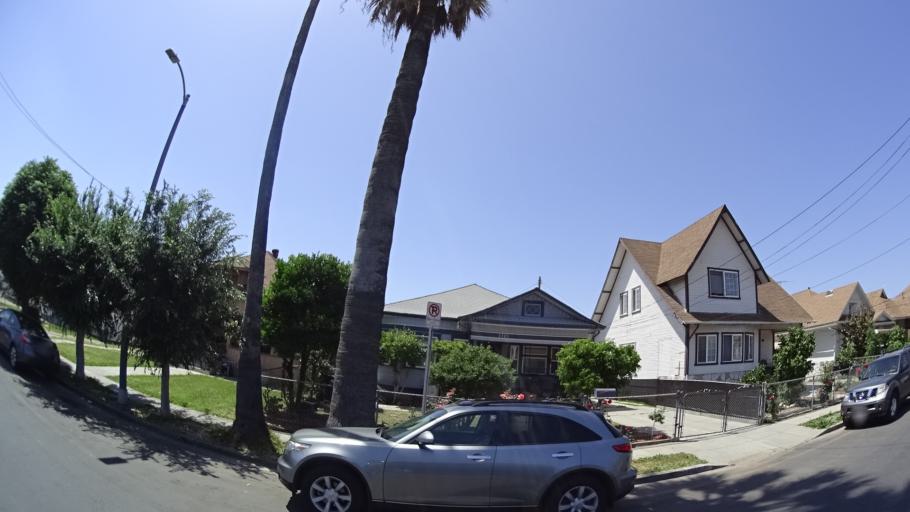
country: US
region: California
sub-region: Los Angeles County
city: Boyle Heights
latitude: 34.0696
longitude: -118.2092
